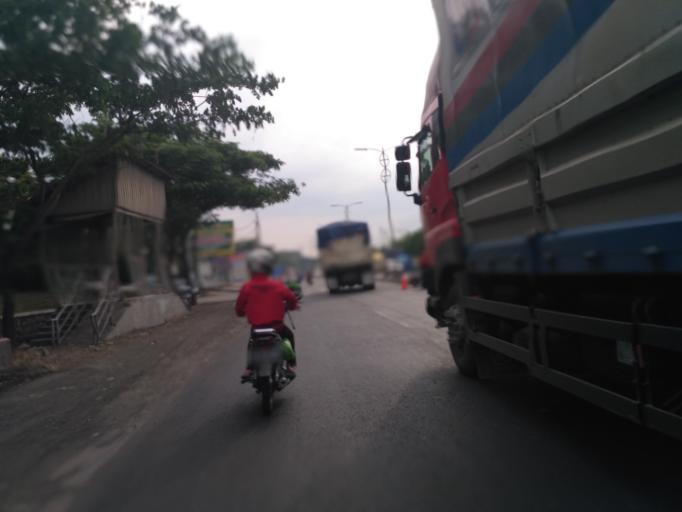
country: ID
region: Central Java
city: Semarang
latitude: -6.9759
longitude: 110.3218
